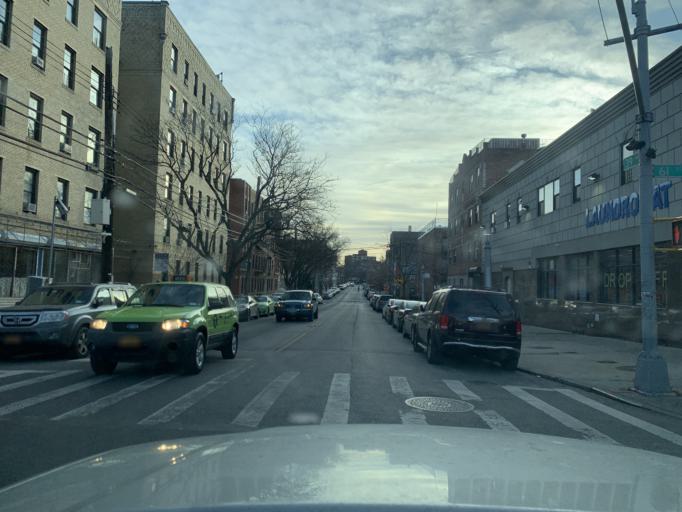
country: US
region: New York
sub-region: Queens County
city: Long Island City
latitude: 40.7472
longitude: -73.9027
